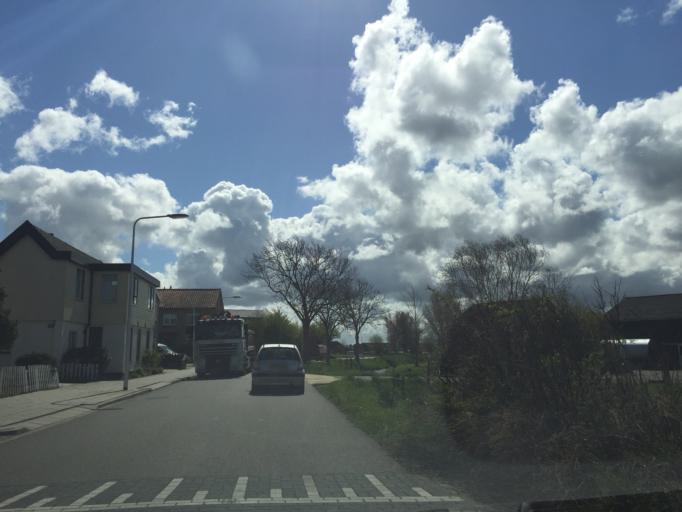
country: NL
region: South Holland
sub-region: Gemeente Kaag en Braassem
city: Oude Wetering
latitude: 52.2057
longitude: 4.6161
